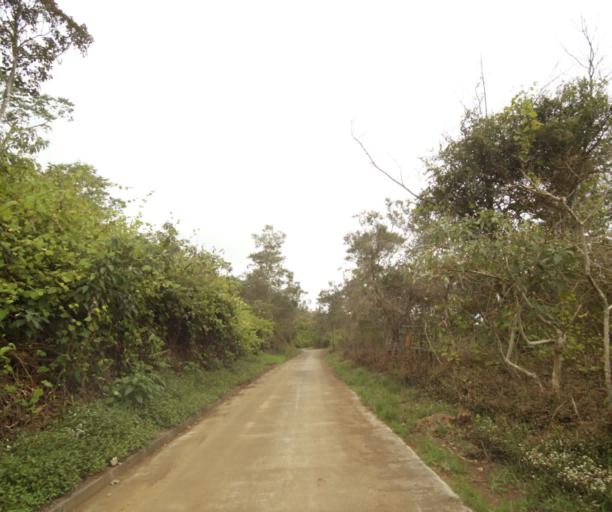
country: RE
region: Reunion
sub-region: Reunion
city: Saint-Paul
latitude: -21.0150
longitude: 55.3560
